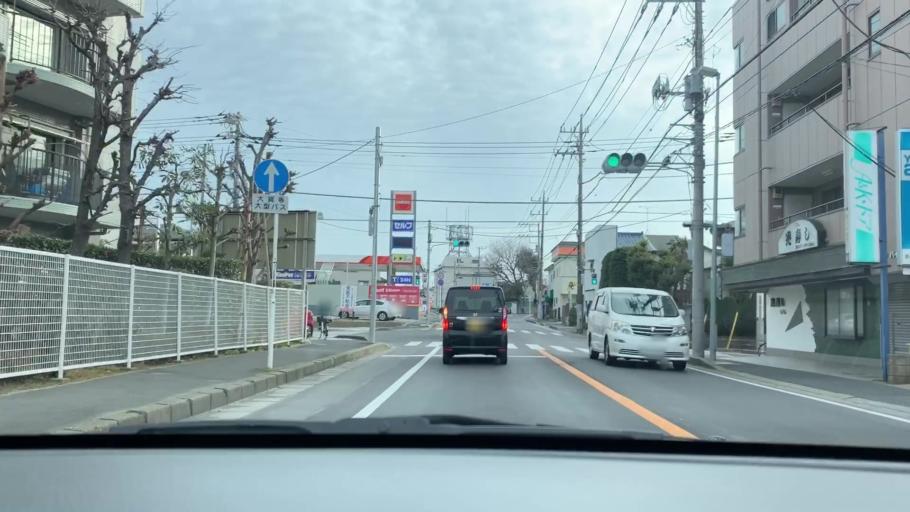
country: JP
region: Chiba
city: Nagareyama
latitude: 35.8575
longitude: 139.9057
